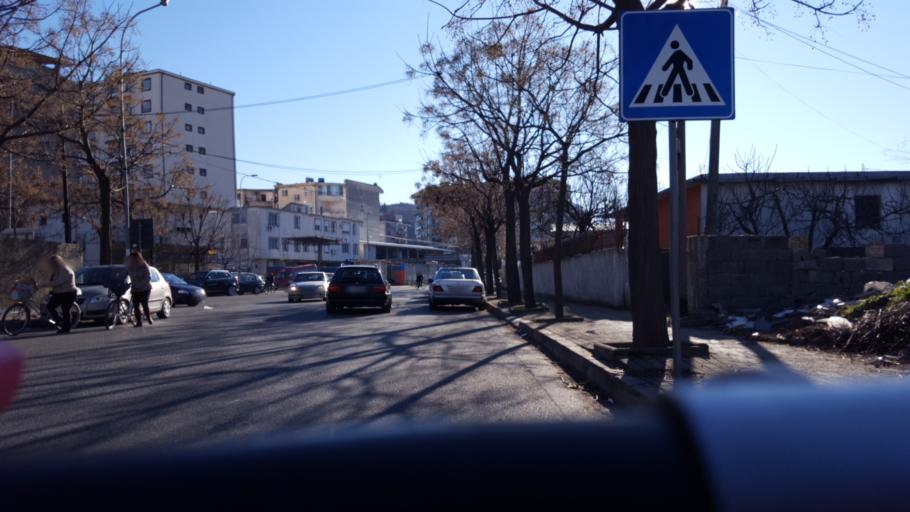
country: AL
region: Shkoder
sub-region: Rrethi i Shkodres
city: Shkoder
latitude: 42.0587
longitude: 19.5007
